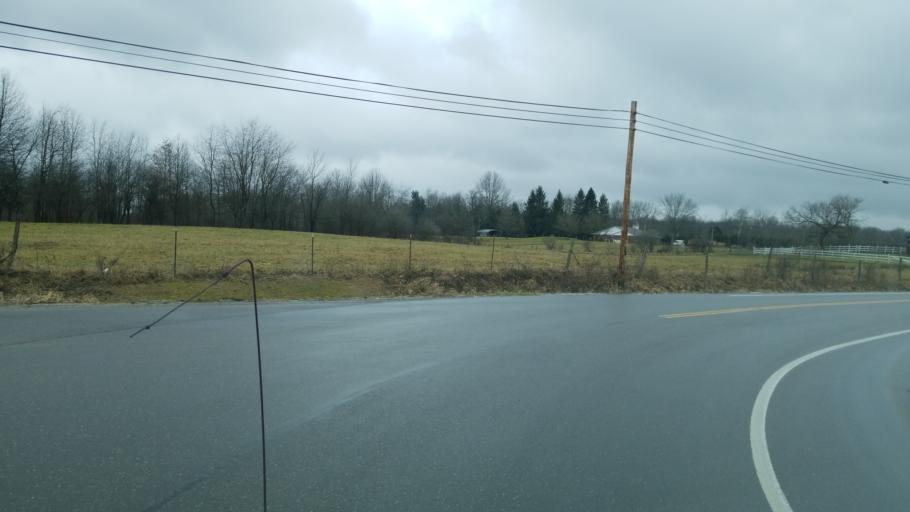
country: US
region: Ohio
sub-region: Trumbull County
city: Champion Heights
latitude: 41.3394
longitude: -80.9545
